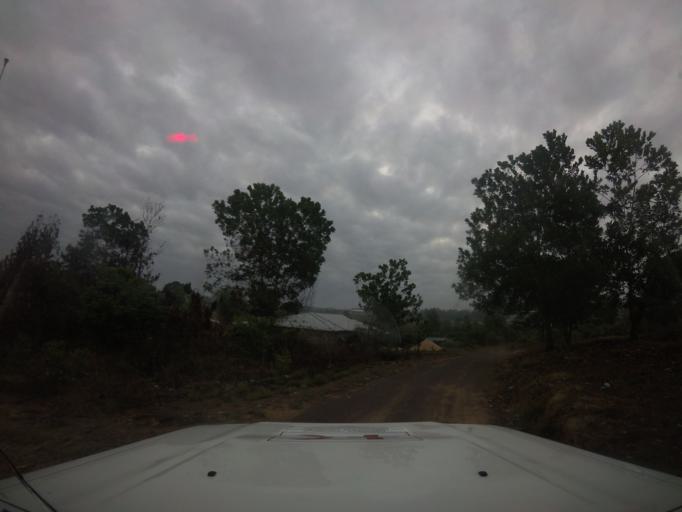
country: LR
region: Bomi
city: Tubmanburg
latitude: 6.8581
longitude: -10.8194
